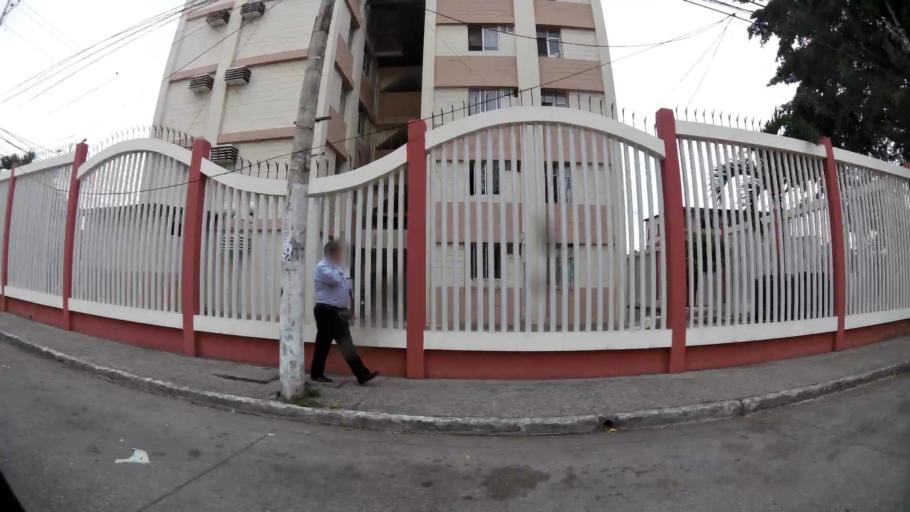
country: EC
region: Guayas
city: Eloy Alfaro
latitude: -2.1267
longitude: -79.8874
